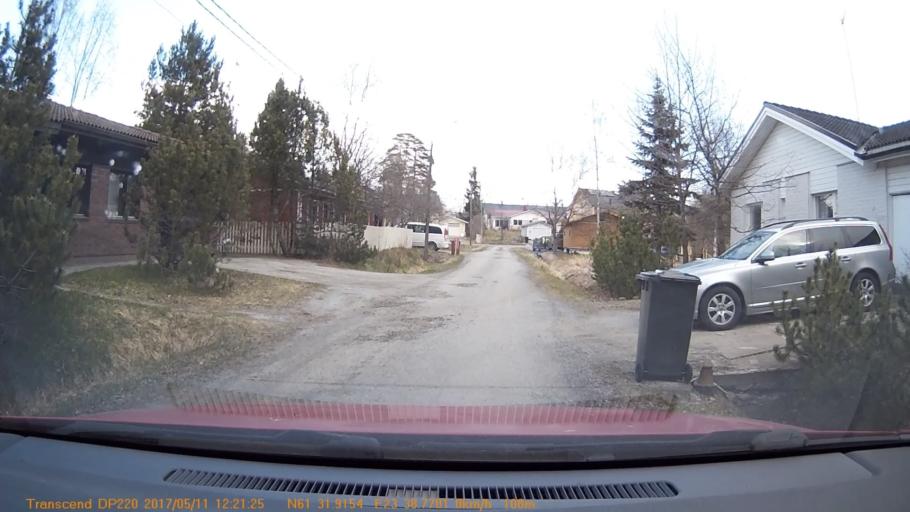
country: FI
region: Pirkanmaa
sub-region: Tampere
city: Yloejaervi
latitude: 61.5319
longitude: 23.6461
